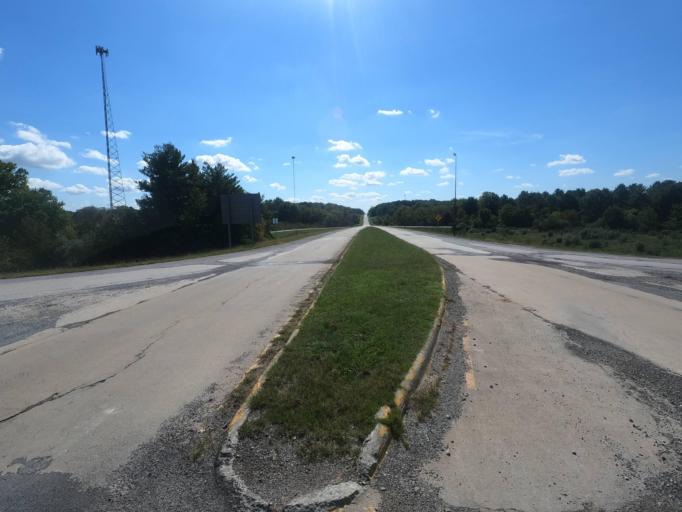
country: US
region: Illinois
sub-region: Jefferson County
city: Mount Vernon
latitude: 38.3599
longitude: -89.0348
